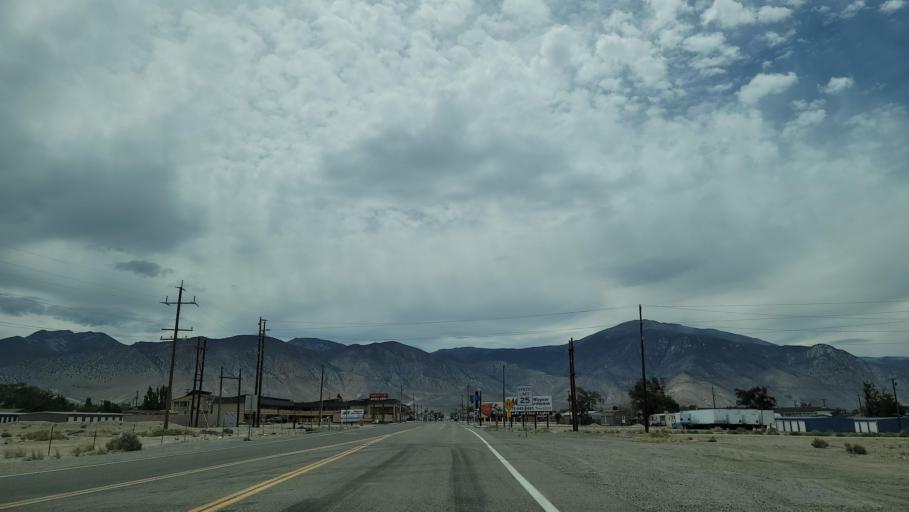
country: US
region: Nevada
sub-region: Mineral County
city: Hawthorne
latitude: 38.5246
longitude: -118.6131
